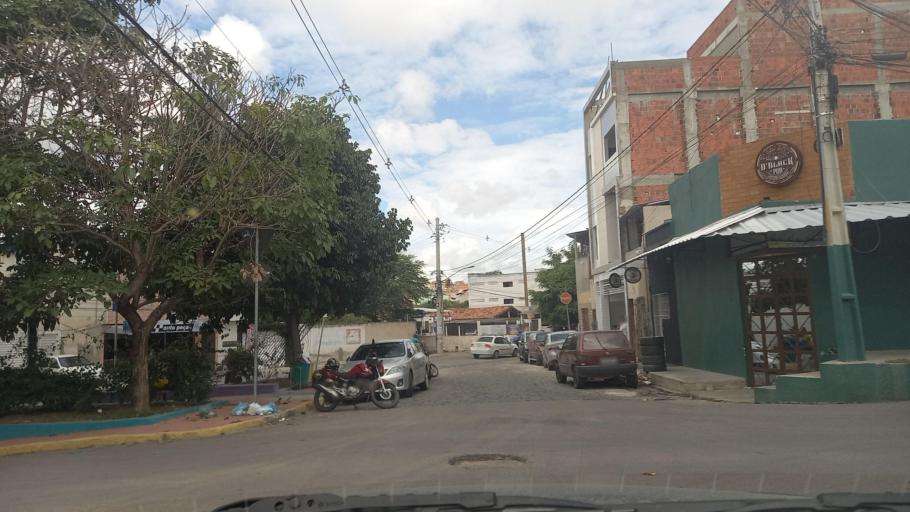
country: BR
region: Pernambuco
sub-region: Caruaru
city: Caruaru
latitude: -8.2709
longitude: -35.9627
